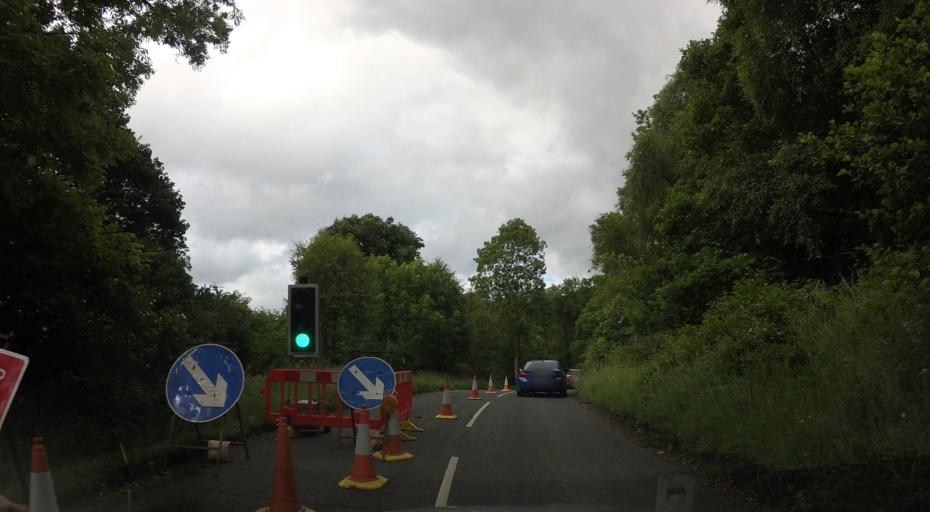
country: GB
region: England
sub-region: Cumbria
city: Keswick
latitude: 54.5486
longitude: -3.1520
